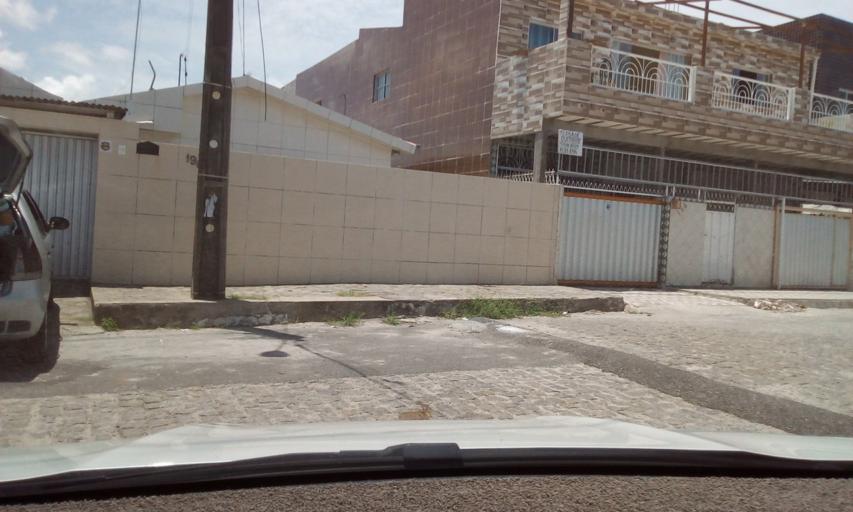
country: BR
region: Paraiba
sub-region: Joao Pessoa
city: Joao Pessoa
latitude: -7.1837
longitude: -34.8440
